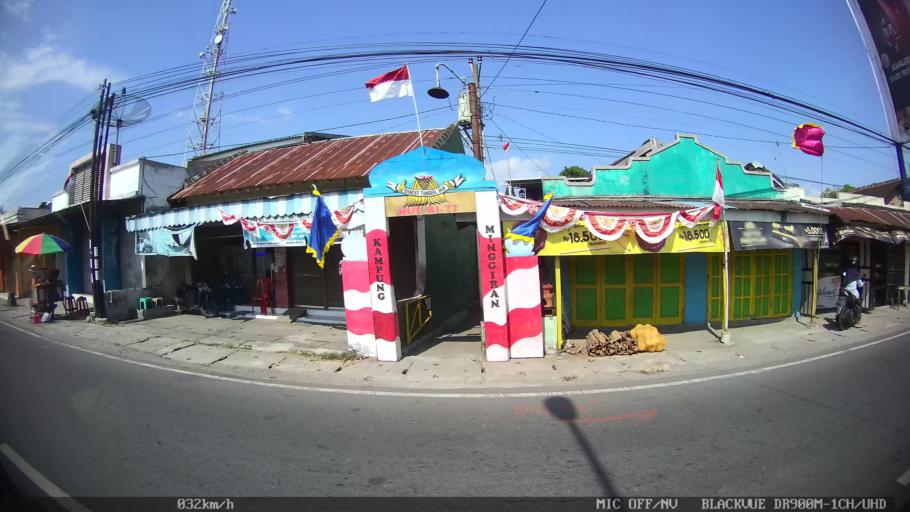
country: ID
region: Daerah Istimewa Yogyakarta
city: Pundong
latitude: -7.9194
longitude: 110.3817
